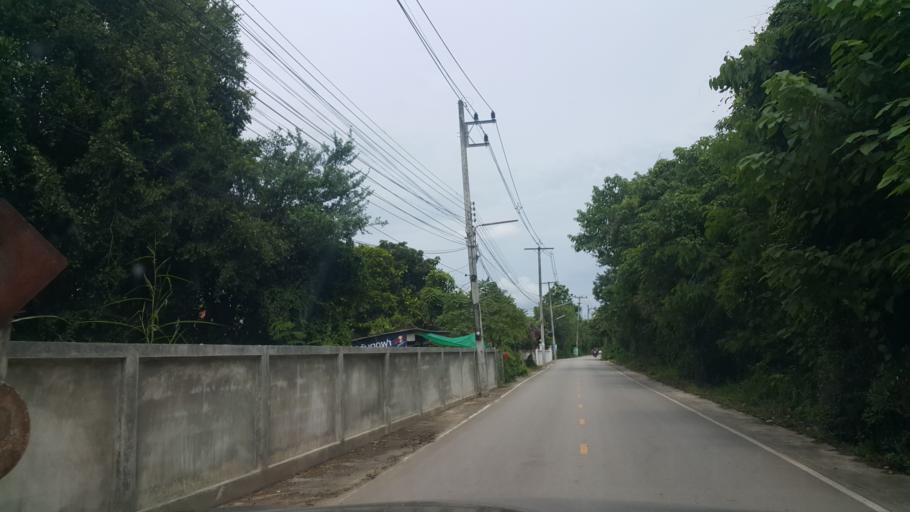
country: TH
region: Chiang Mai
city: San Kamphaeng
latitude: 18.7506
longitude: 99.1365
